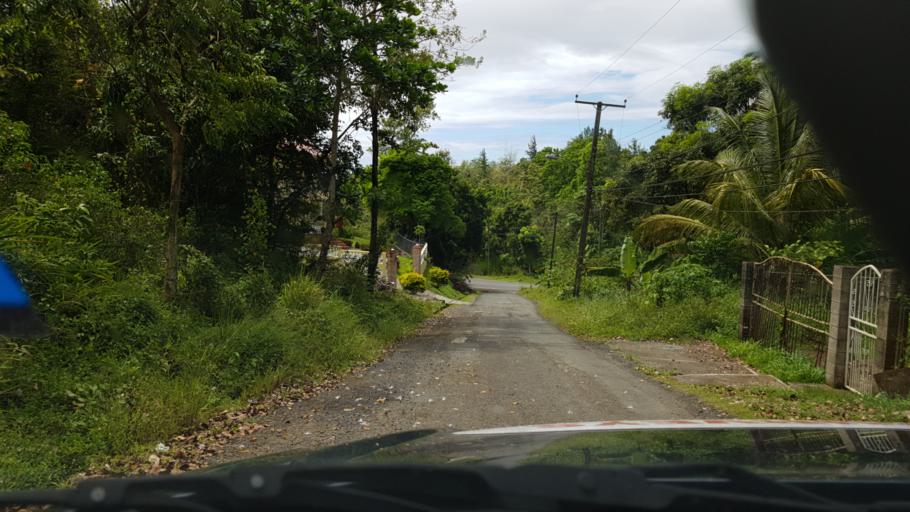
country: LC
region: Anse-la-Raye
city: Anse La Raye
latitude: 13.9500
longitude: -61.0355
